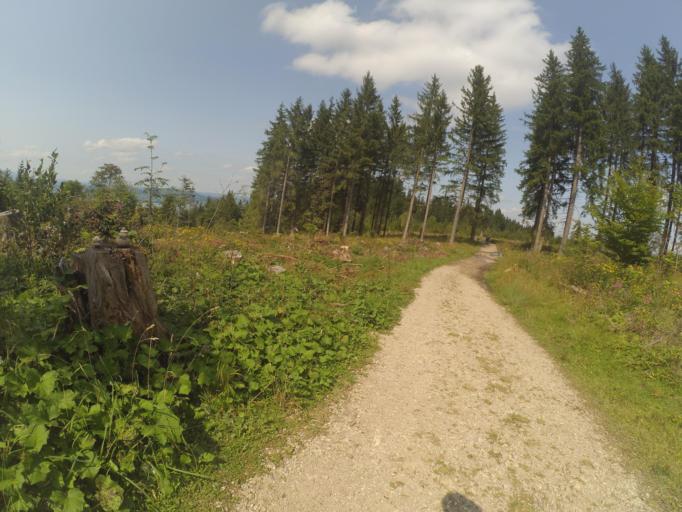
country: DE
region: Bavaria
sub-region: Swabia
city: Halblech
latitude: 47.6029
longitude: 10.8123
